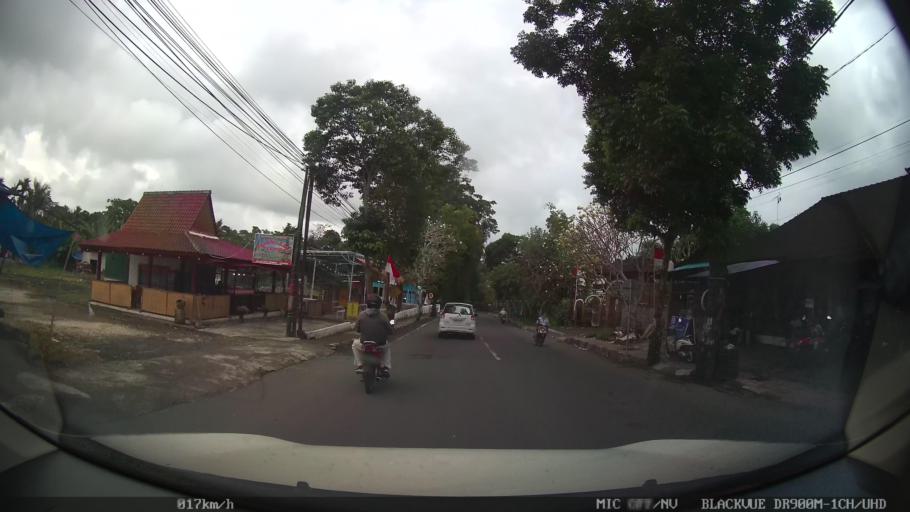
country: ID
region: Bali
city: Banjar Mambalkajanan
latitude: -8.5482
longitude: 115.2186
